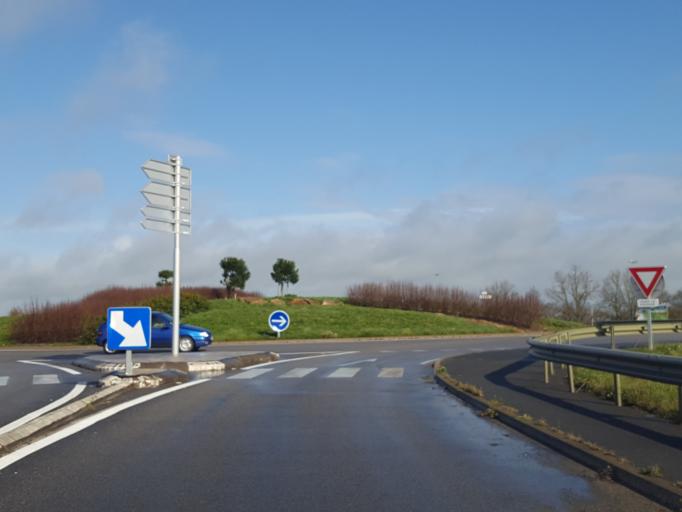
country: FR
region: Pays de la Loire
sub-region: Departement de la Vendee
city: Saligny
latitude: 46.7980
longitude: -1.4288
